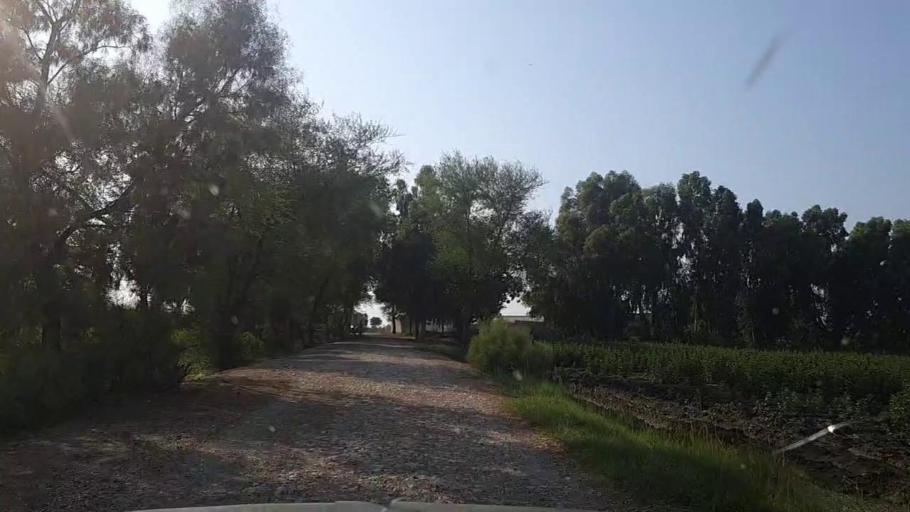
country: PK
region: Sindh
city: Khanpur
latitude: 27.7064
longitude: 69.3329
